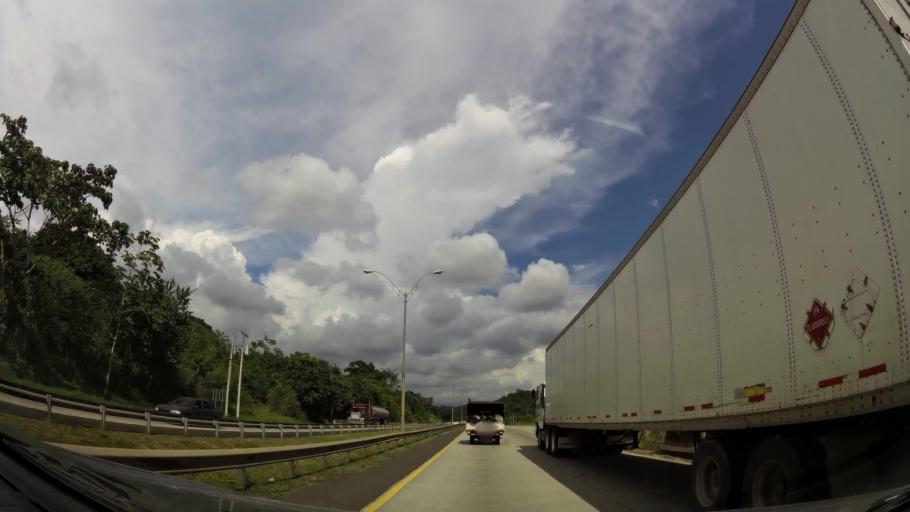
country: PA
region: Panama
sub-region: Distrito de Panama
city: Paraiso
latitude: 9.0322
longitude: -79.5822
